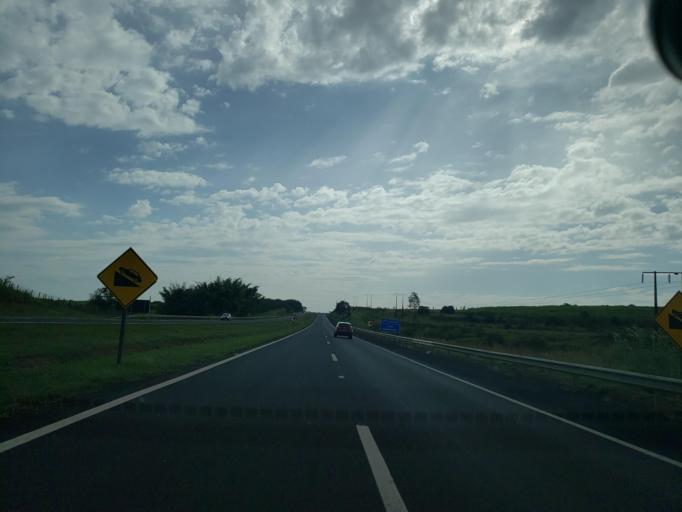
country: BR
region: Sao Paulo
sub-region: Lins
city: Lins
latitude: -21.7419
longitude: -49.6972
